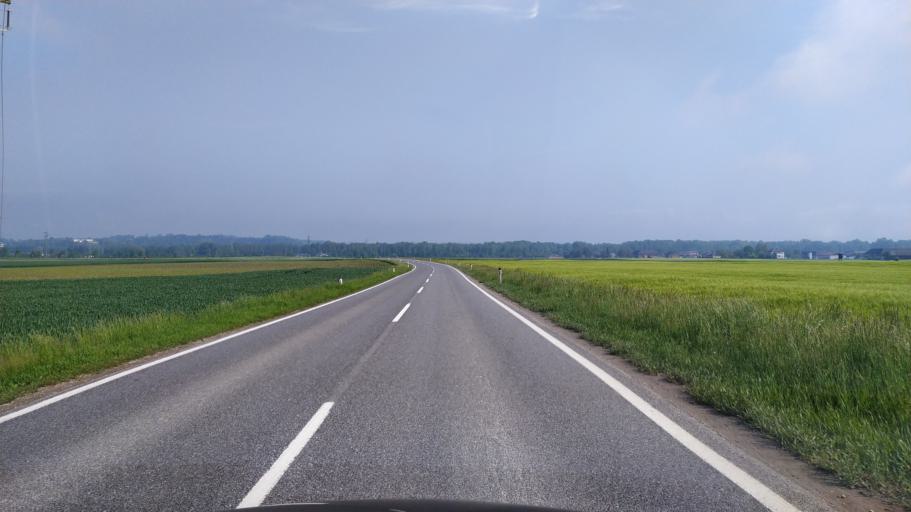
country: AT
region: Lower Austria
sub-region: Politischer Bezirk Amstetten
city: Ennsdorf
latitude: 48.2198
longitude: 14.5396
